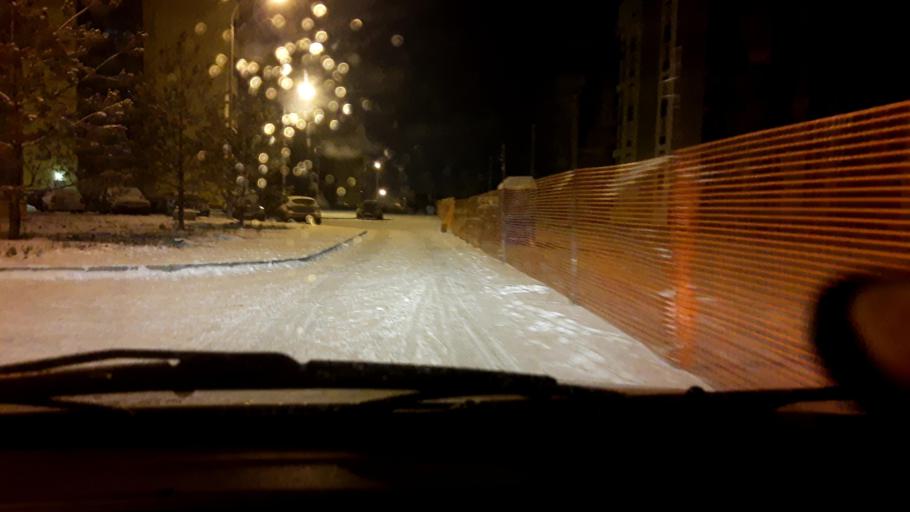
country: RU
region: Bashkortostan
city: Ufa
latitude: 54.7974
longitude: 55.9517
